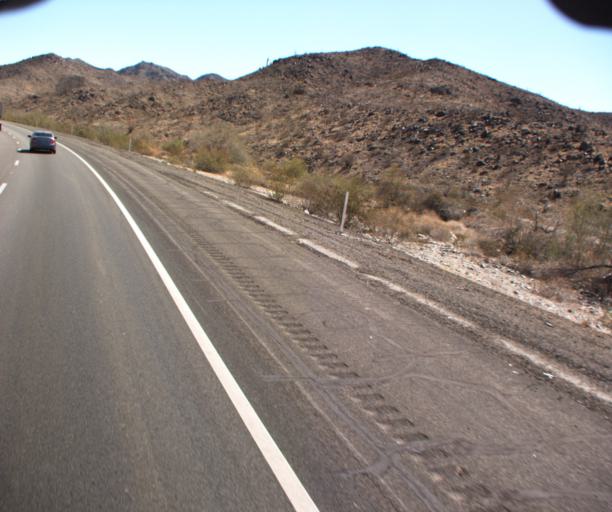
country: US
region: Arizona
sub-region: Yuma County
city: Fortuna Foothills
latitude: 32.6579
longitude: -114.3443
